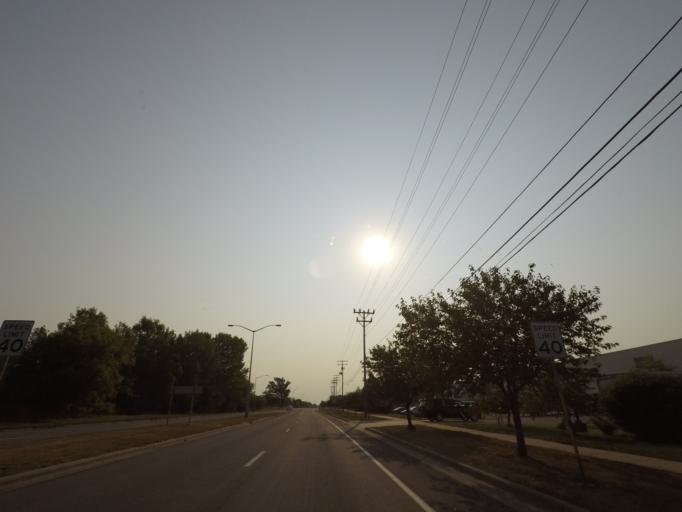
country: US
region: Wisconsin
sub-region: Dane County
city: McFarland
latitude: 43.0516
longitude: -89.2905
